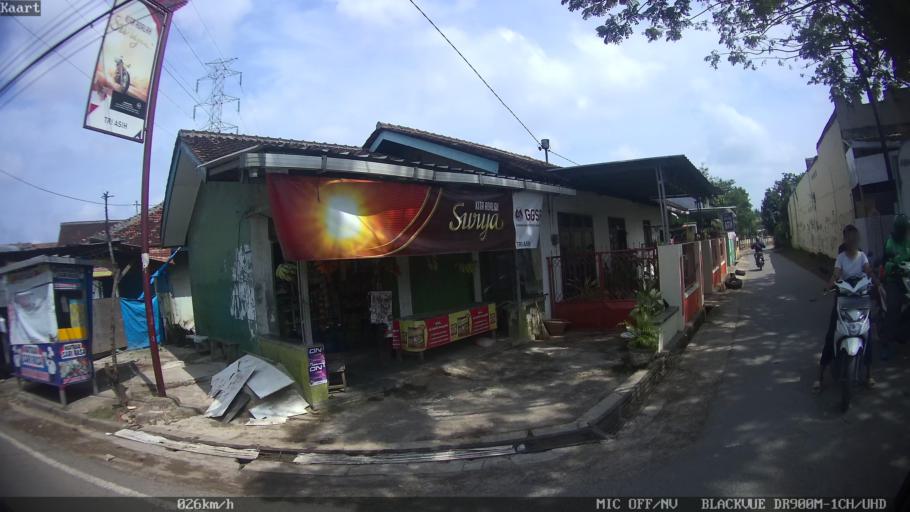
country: ID
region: Lampung
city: Kedaton
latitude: -5.3548
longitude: 105.2881
